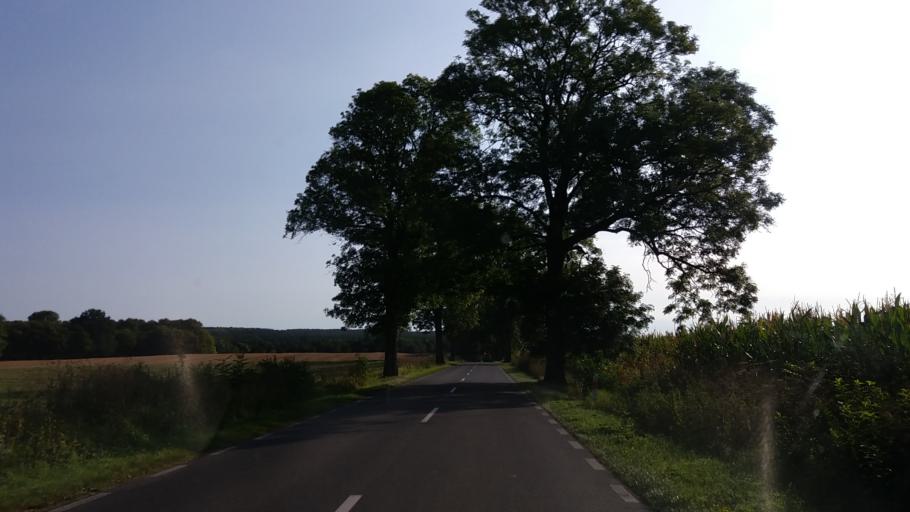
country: PL
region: West Pomeranian Voivodeship
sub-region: Powiat choszczenski
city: Choszczno
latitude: 53.1782
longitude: 15.5071
